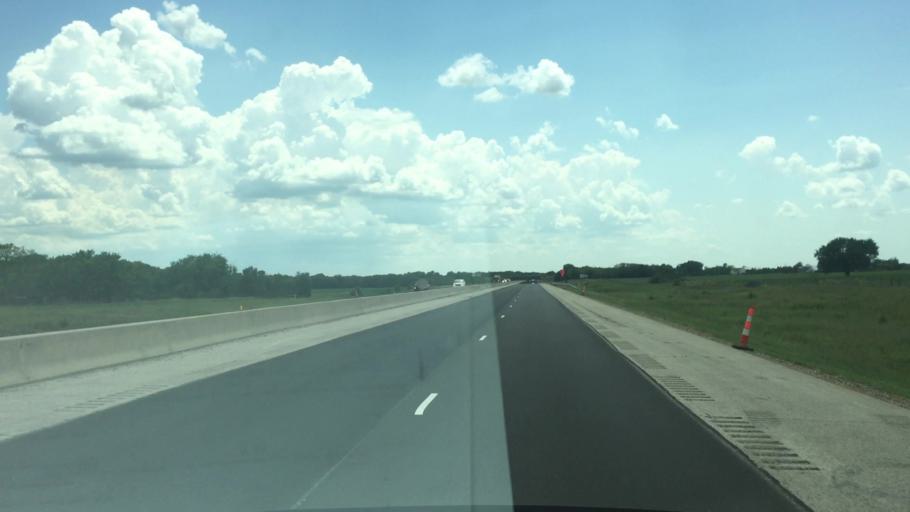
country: US
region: Kansas
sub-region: Lyon County
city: Emporia
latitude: 38.5157
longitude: -96.1451
